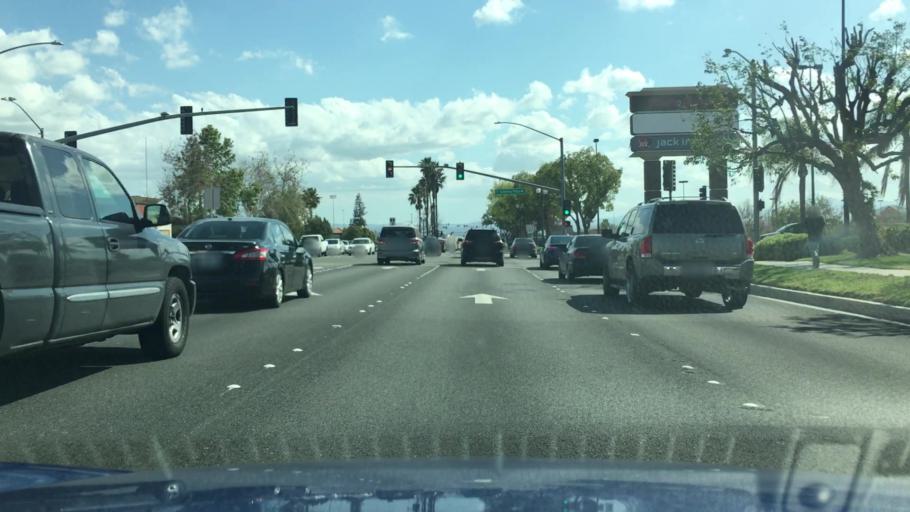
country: US
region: California
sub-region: San Bernardino County
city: Bloomington
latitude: 34.0734
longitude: -117.3704
